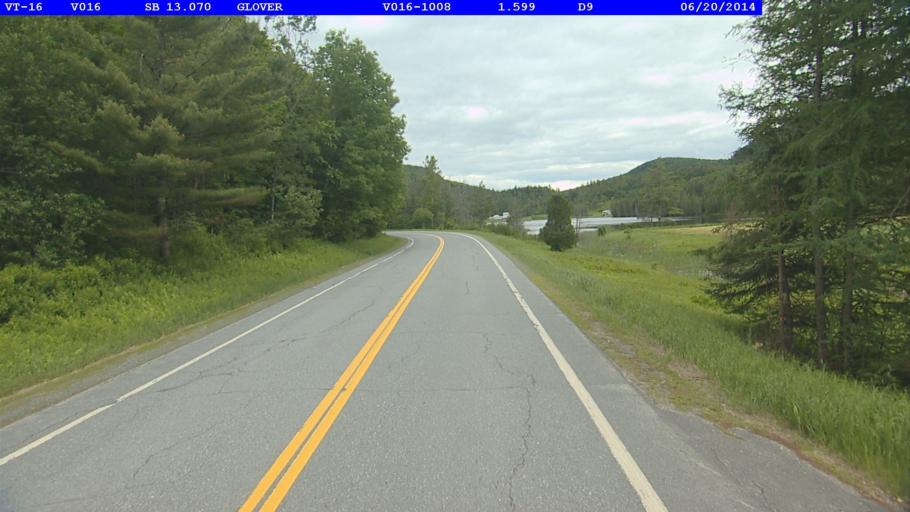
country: US
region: Vermont
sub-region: Caledonia County
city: Hardwick
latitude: 44.6479
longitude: -72.2015
